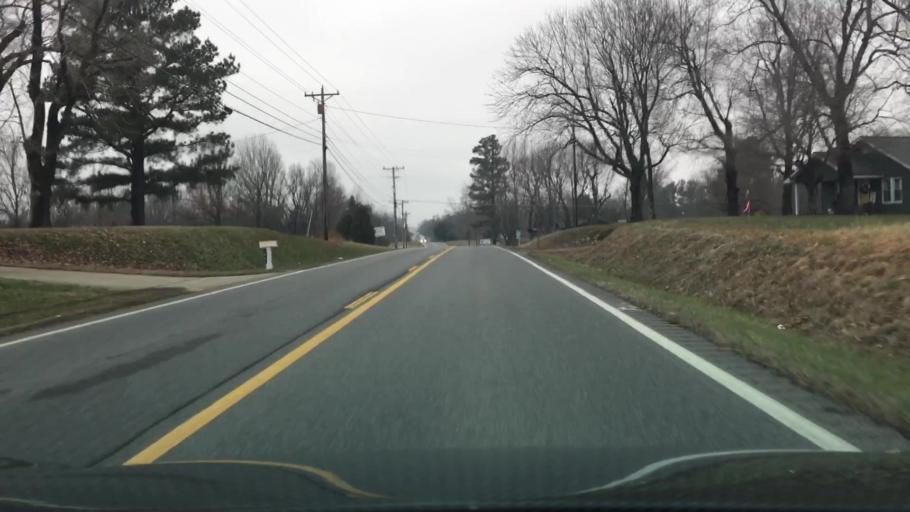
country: US
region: Kentucky
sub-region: McCracken County
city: Reidland
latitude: 36.9838
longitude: -88.4916
